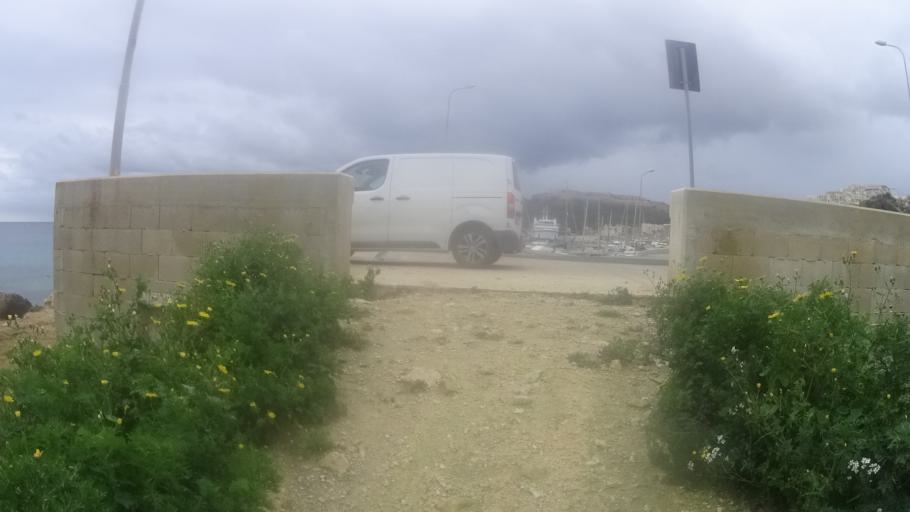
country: MT
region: Ghajnsielem
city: Mgarr
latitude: 36.0275
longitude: 14.3025
